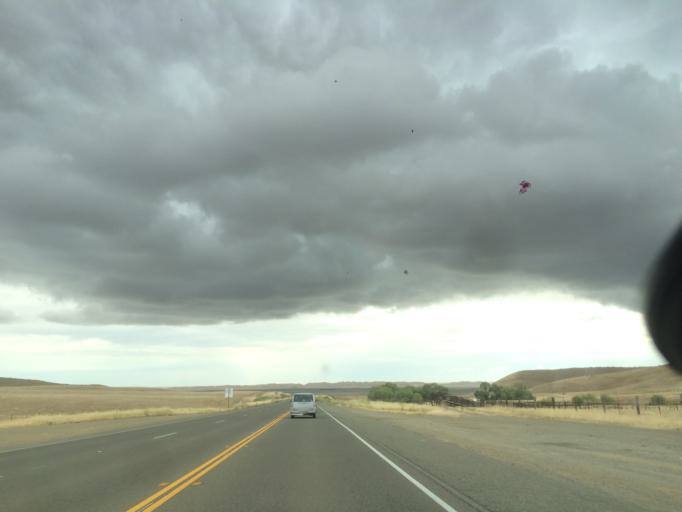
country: US
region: California
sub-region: Kings County
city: Avenal
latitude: 35.7771
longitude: -120.1367
